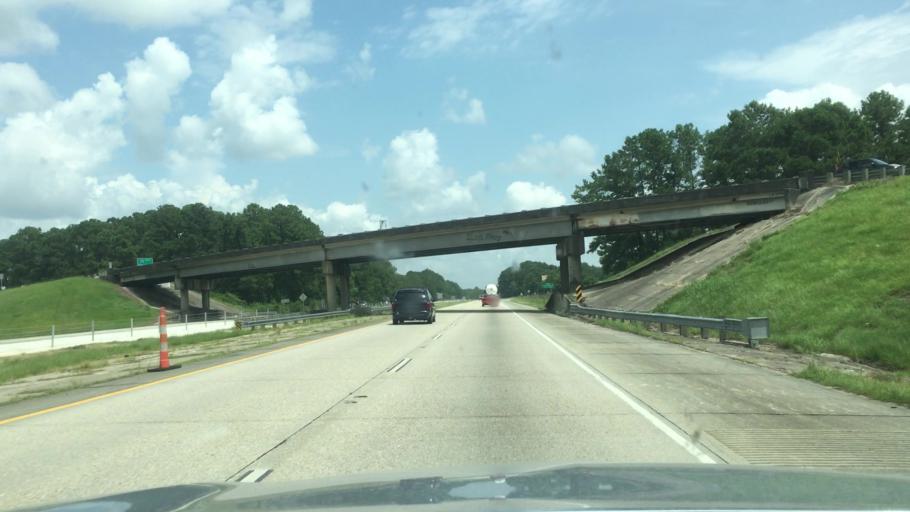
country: US
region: Louisiana
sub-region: Saint Tammany Parish
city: Pearl River
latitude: 30.3525
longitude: -89.7403
